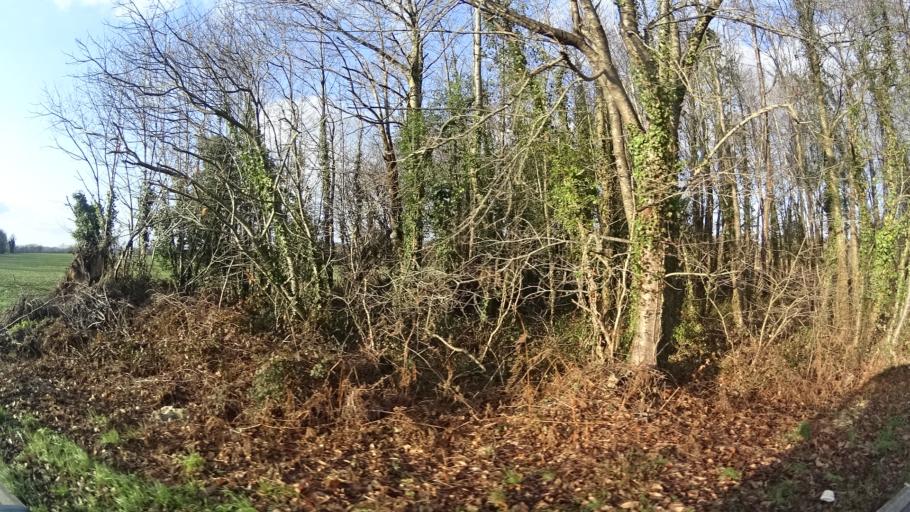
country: FR
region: Pays de la Loire
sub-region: Departement de la Loire-Atlantique
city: Saint-Nicolas-de-Redon
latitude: 47.6303
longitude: -2.0551
